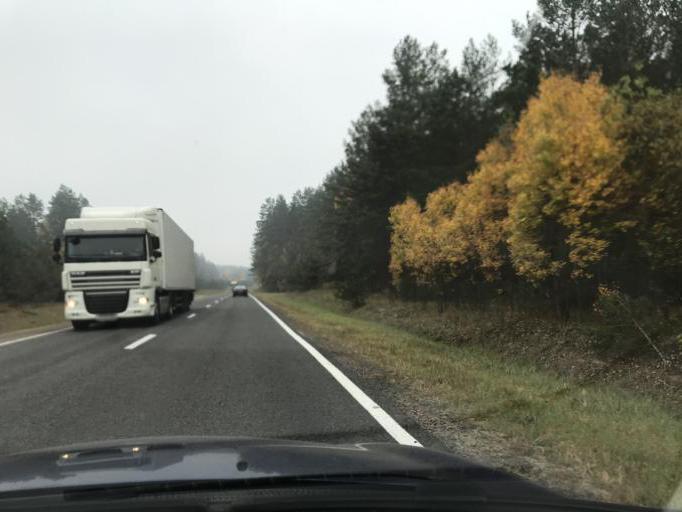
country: LT
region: Alytaus apskritis
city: Druskininkai
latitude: 53.8914
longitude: 23.9111
